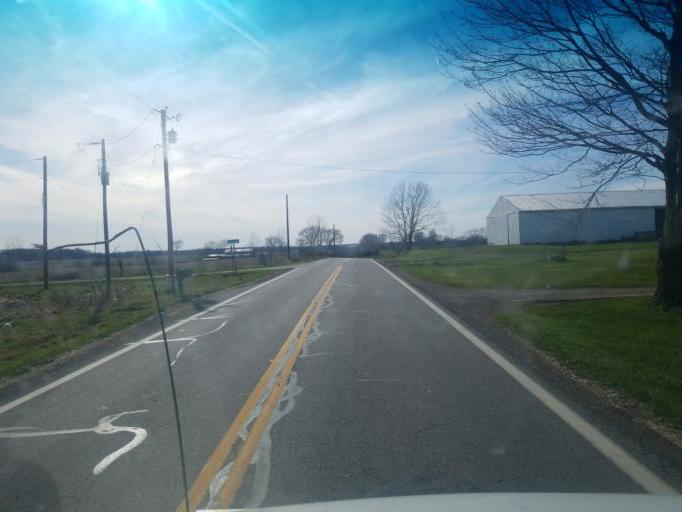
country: US
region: Ohio
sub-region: Champaign County
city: North Lewisburg
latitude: 40.3411
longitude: -83.4875
